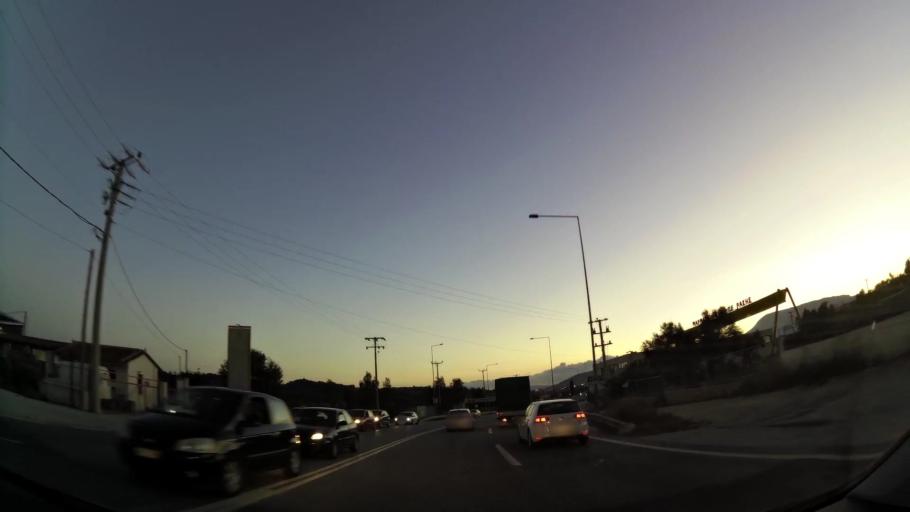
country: GR
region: Attica
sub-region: Nomarchia Anatolikis Attikis
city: Pikermi
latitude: 37.9970
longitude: 23.9234
